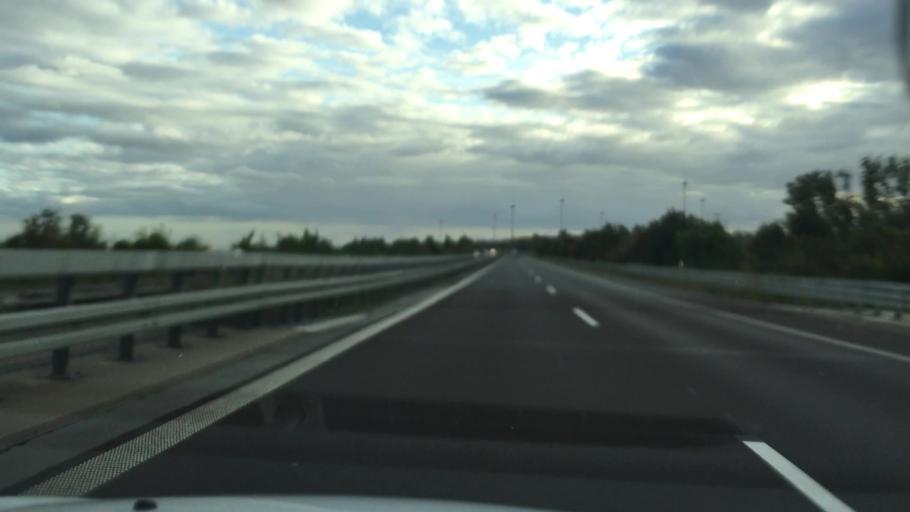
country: DE
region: Saxony-Anhalt
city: Ilberstedt
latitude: 51.7896
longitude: 11.6770
